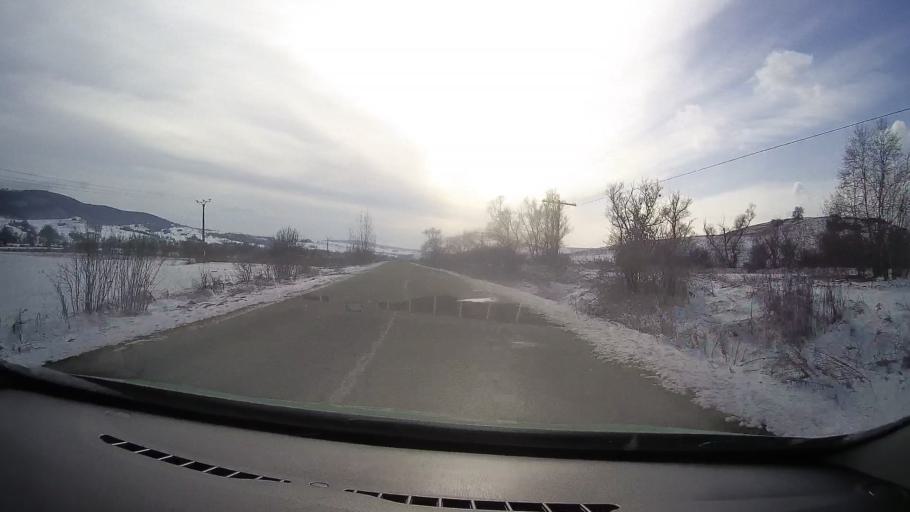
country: RO
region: Sibiu
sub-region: Comuna Iacobeni
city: Iacobeni
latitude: 46.0306
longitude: 24.7145
